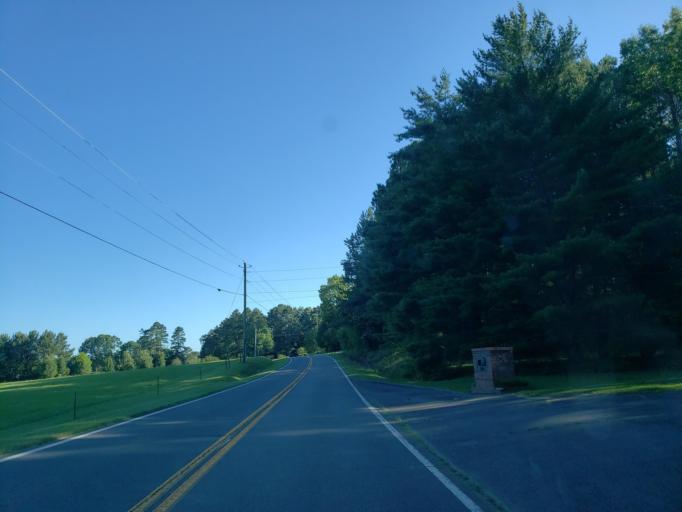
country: US
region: Georgia
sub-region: Floyd County
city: Shannon
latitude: 34.3708
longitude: -85.1319
